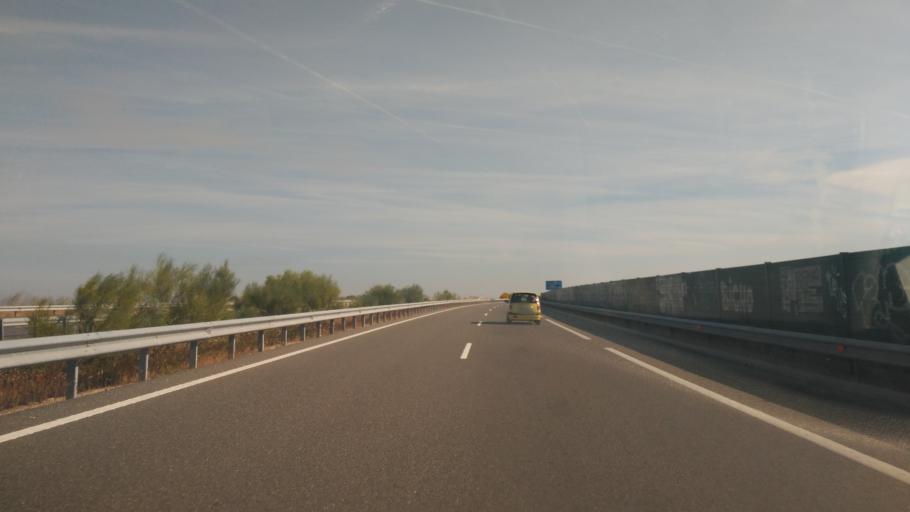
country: ES
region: Castille and Leon
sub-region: Provincia de Salamanca
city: Villamayor
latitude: 41.0185
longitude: -5.6799
